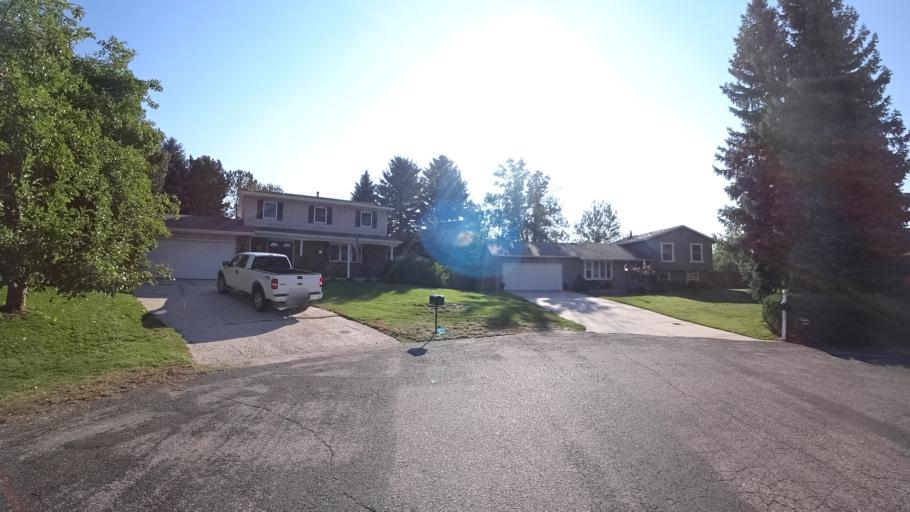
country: US
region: Colorado
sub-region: El Paso County
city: Air Force Academy
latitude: 38.9307
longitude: -104.7825
